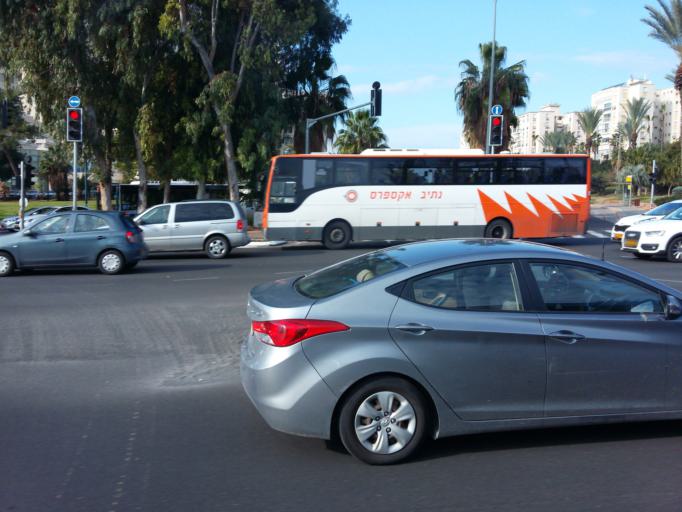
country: IL
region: Tel Aviv
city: Tel Aviv
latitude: 32.1023
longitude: 34.7919
